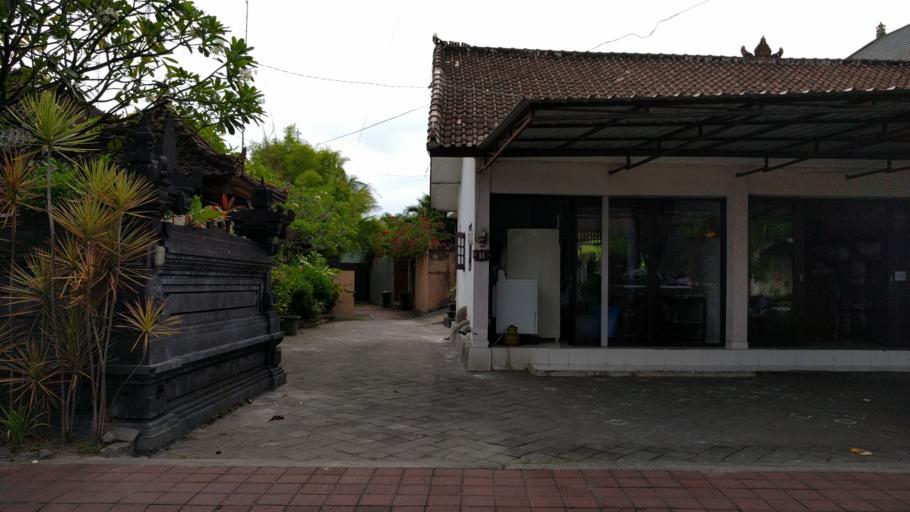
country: ID
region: Bali
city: Kuta
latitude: -8.6822
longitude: 115.1673
